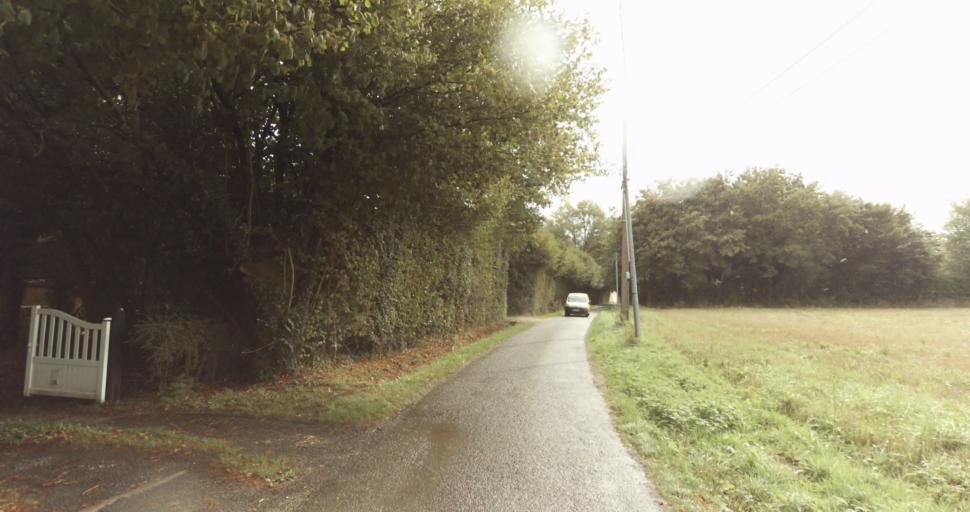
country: FR
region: Lower Normandy
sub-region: Departement de l'Orne
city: Sainte-Gauburge-Sainte-Colombe
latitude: 48.6879
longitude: 0.4103
